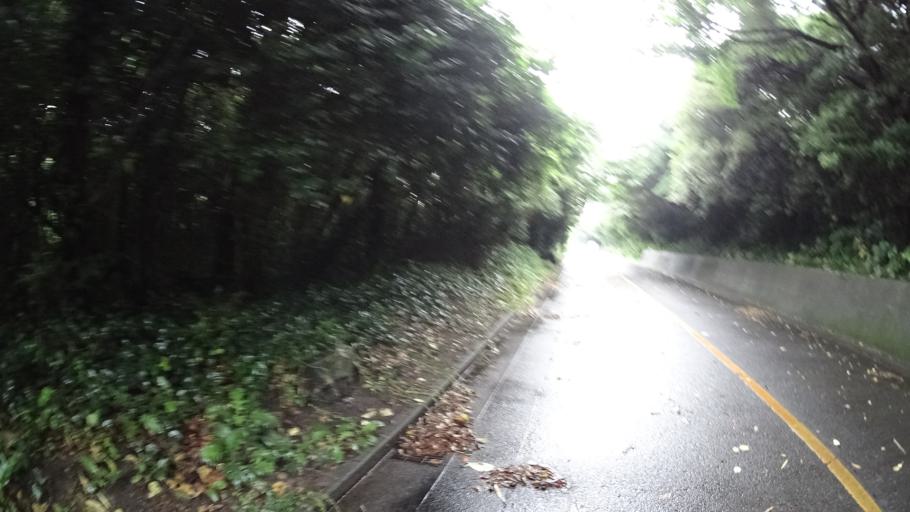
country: JP
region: Shizuoka
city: Shimoda
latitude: 34.3323
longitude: 139.2132
